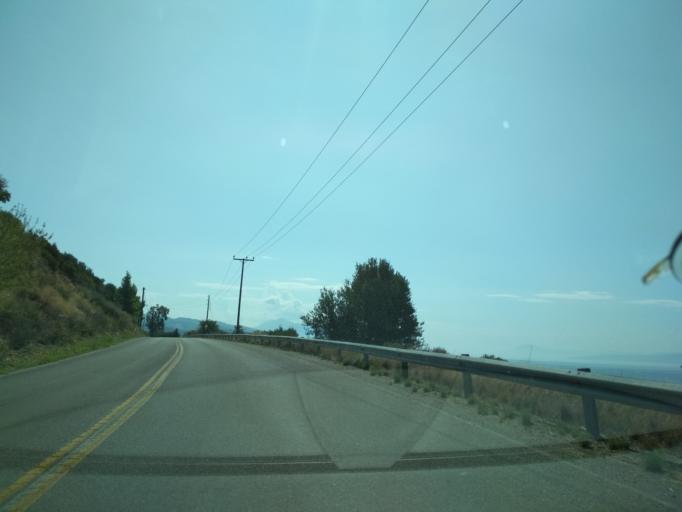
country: GR
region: Central Greece
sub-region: Nomos Evvoias
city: Roviai
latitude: 38.8387
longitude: 23.1788
